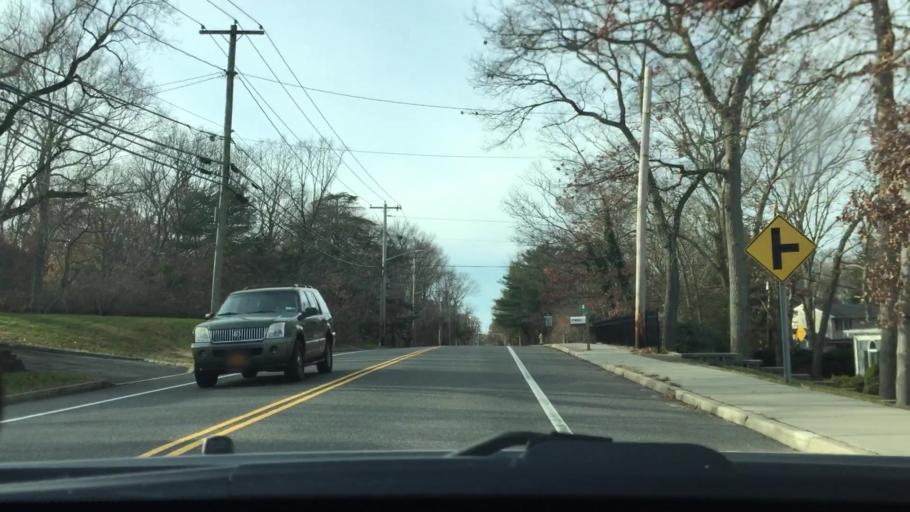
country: US
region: New York
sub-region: Suffolk County
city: Port Jefferson Station
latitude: 40.9189
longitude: -73.0228
